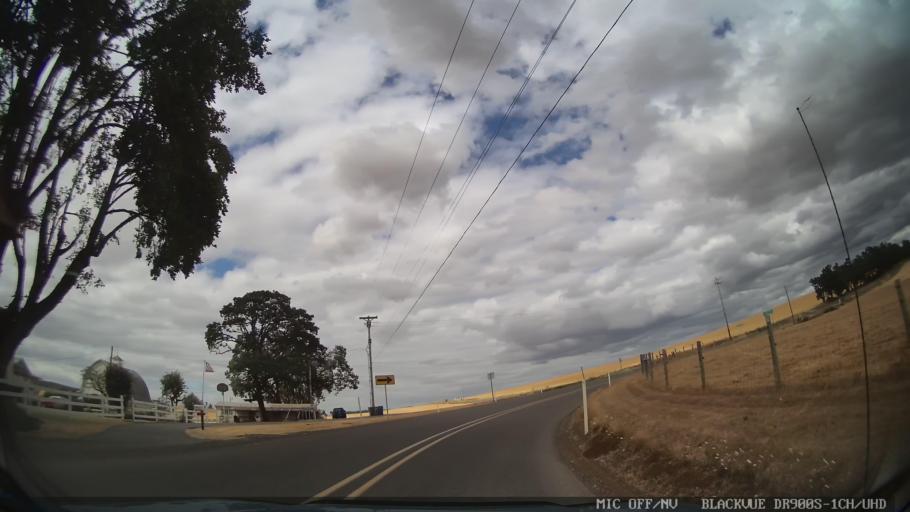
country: US
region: Oregon
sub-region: Marion County
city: Sublimity
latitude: 44.8671
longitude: -122.7556
